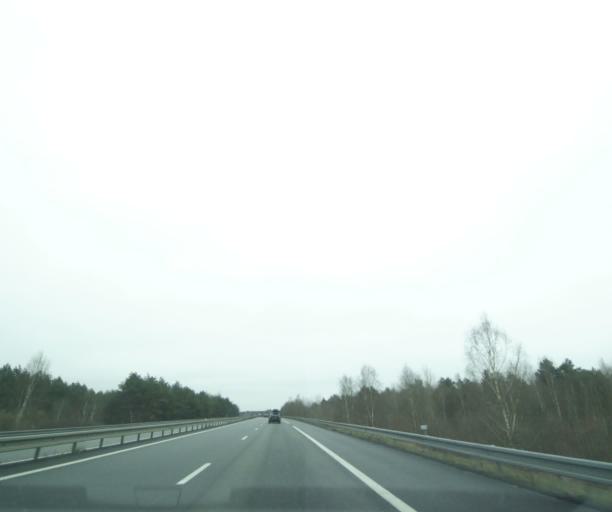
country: FR
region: Centre
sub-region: Departement du Loir-et-Cher
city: Salbris
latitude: 47.4091
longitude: 2.0257
